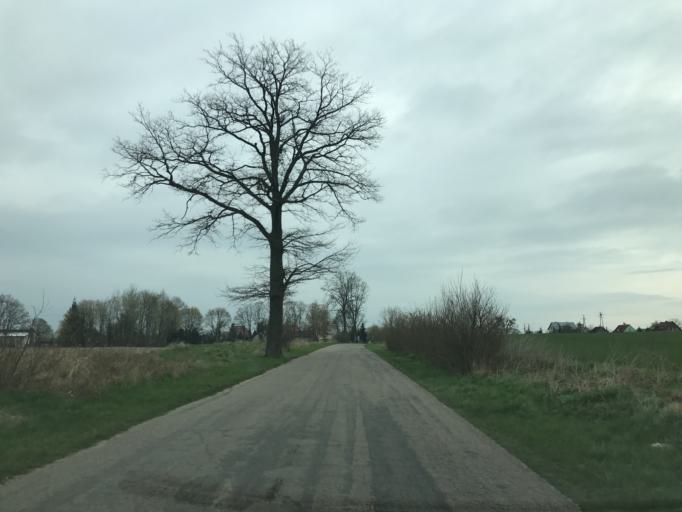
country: PL
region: Warmian-Masurian Voivodeship
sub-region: Powiat ostrodzki
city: Gierzwald
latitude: 53.6454
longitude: 20.0991
